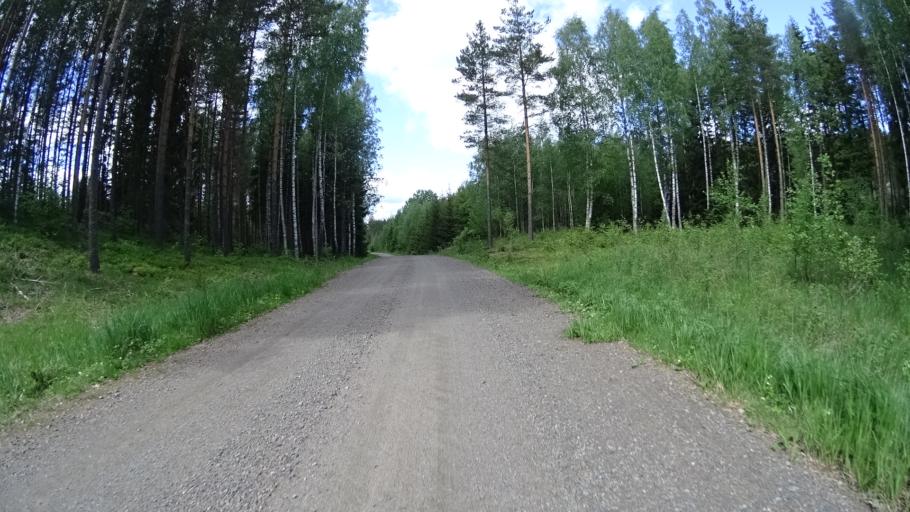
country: FI
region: Uusimaa
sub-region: Raaseporin
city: Karis
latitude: 60.1381
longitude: 23.6242
